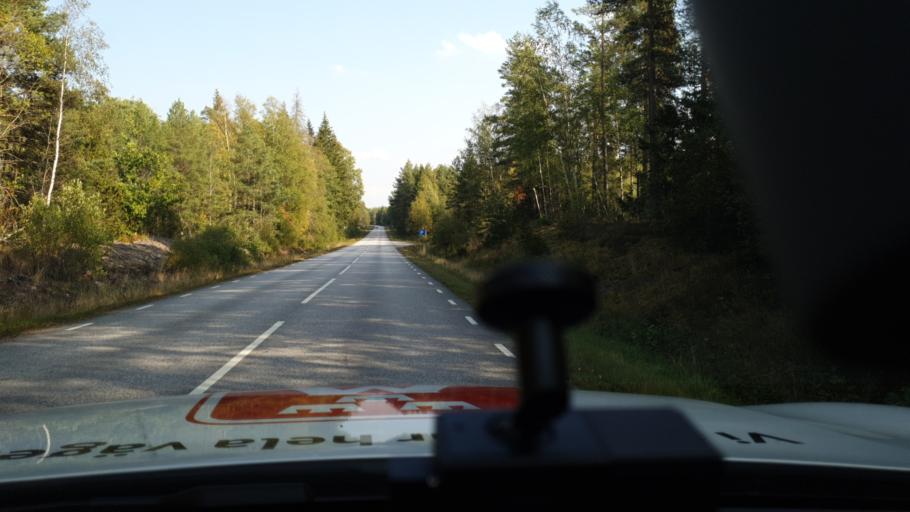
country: SE
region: Kalmar
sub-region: Vimmerby Kommun
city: Vimmerby
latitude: 57.5868
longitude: 15.9781
